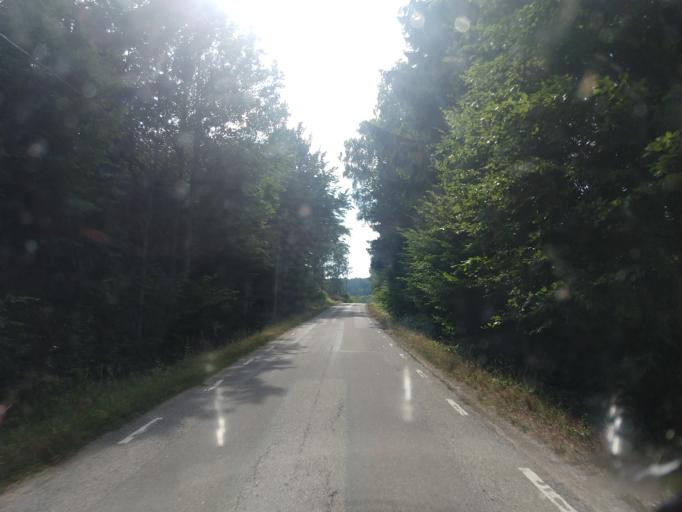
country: SE
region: Blekinge
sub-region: Karlskrona Kommun
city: Nattraby
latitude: 56.2571
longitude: 15.5198
